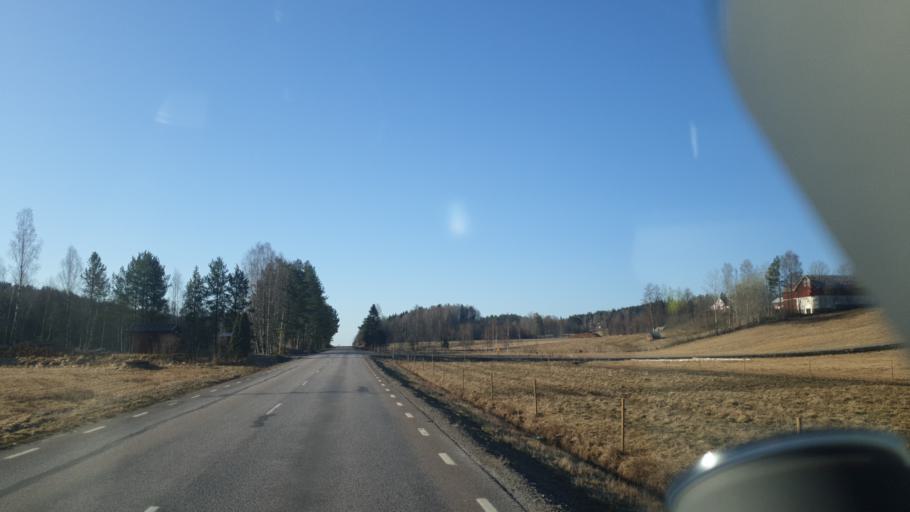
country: SE
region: Vaermland
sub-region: Arvika Kommun
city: Arvika
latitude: 59.7438
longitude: 12.6395
